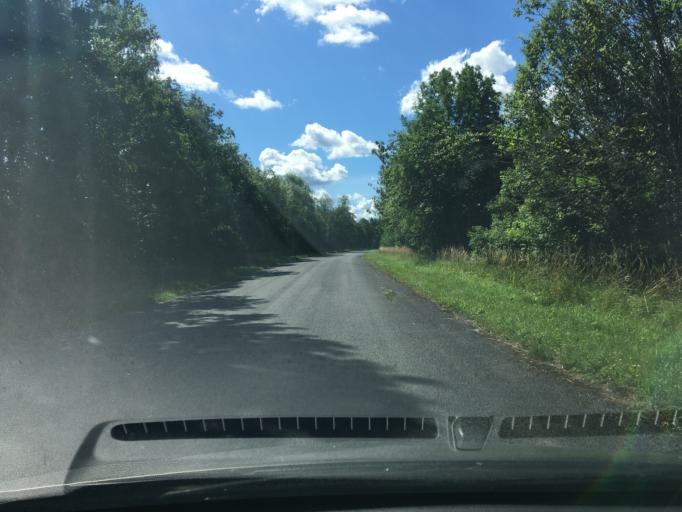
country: EE
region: Laeaene
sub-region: Lihula vald
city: Lihula
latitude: 58.7346
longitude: 23.9945
